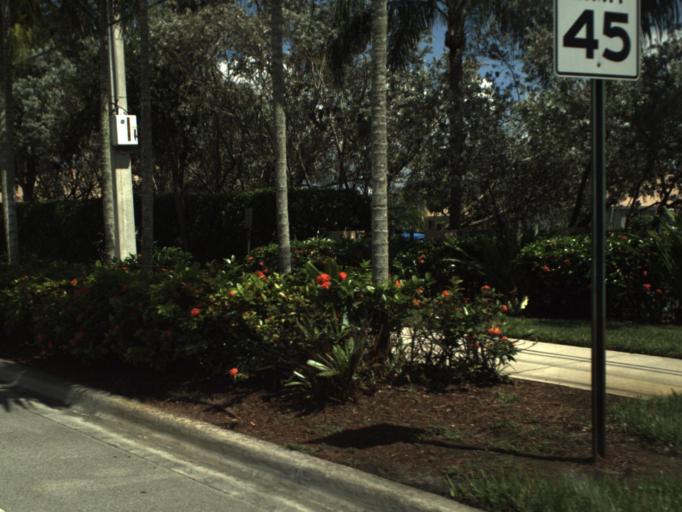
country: US
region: Florida
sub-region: Miami-Dade County
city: Country Club
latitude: 25.9931
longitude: -80.3041
